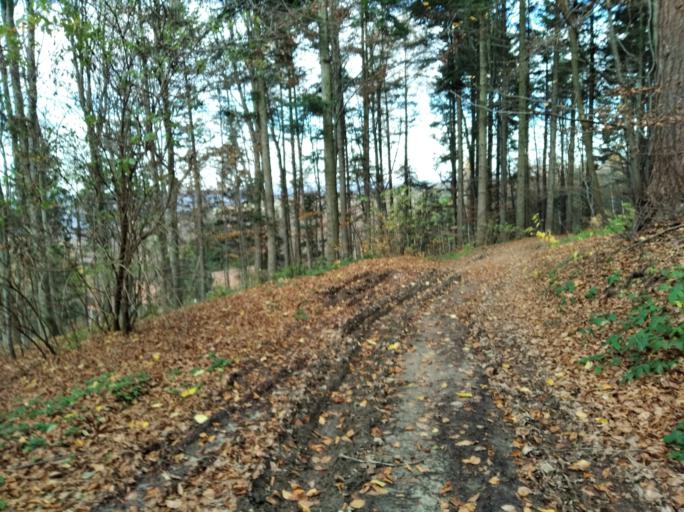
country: PL
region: Subcarpathian Voivodeship
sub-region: Powiat strzyzowski
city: Jawornik
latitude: 49.8534
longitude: 21.8483
